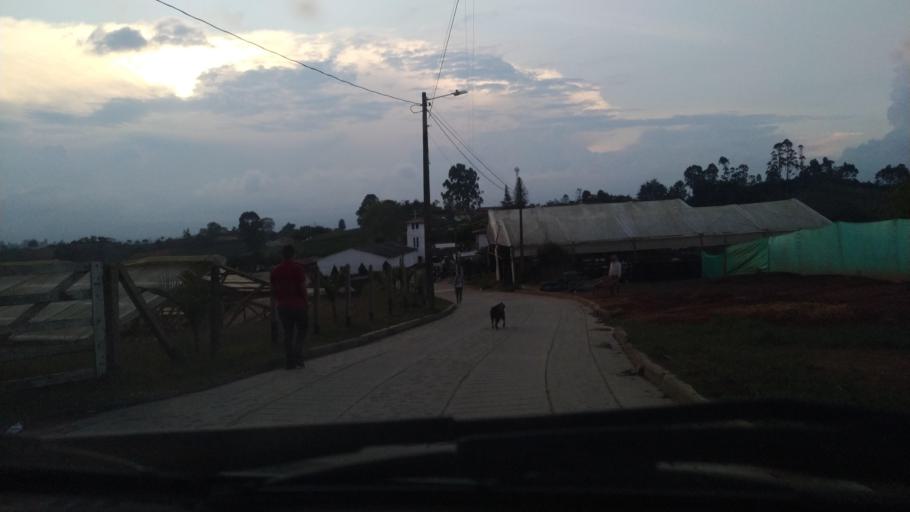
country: CO
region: Antioquia
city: Marinilla
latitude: 6.1937
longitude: -75.2858
